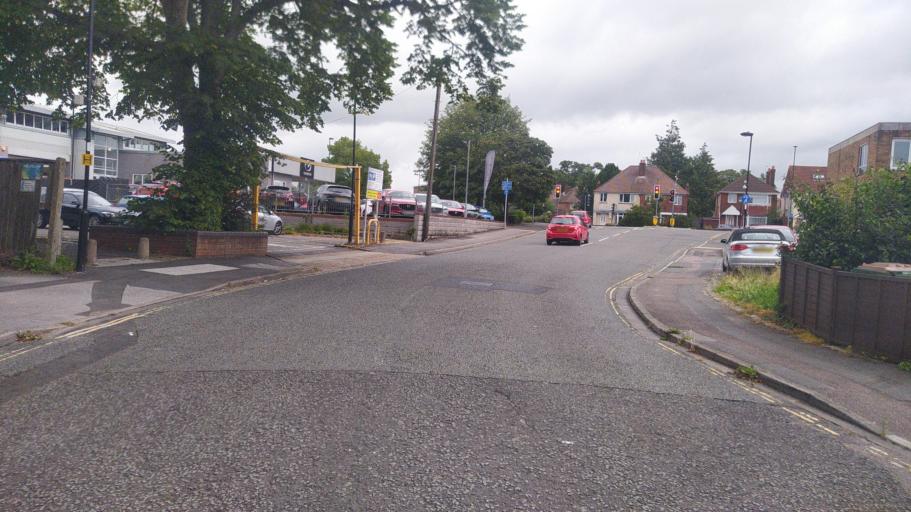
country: GB
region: England
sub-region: Hampshire
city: West End
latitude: 50.9129
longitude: -1.3568
